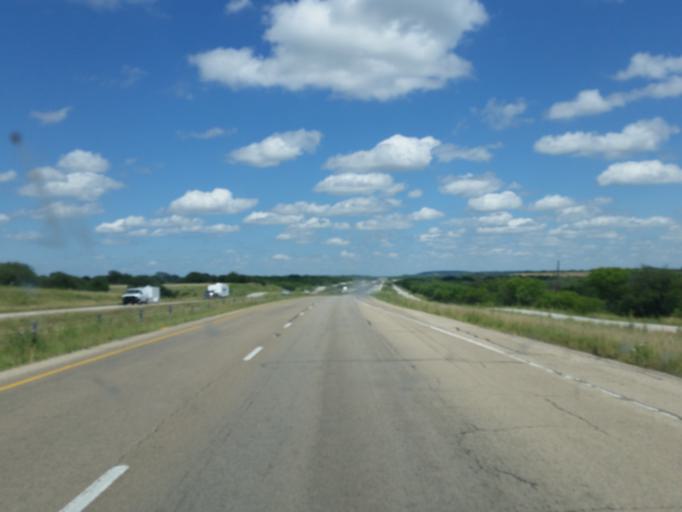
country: US
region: Texas
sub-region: Callahan County
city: Baird
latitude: 32.3851
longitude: -99.2924
